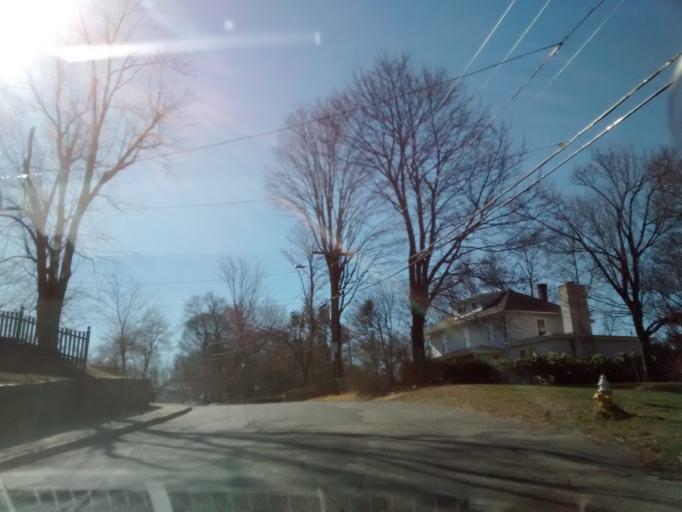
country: US
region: Massachusetts
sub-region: Worcester County
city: Worcester
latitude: 42.2965
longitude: -71.8200
